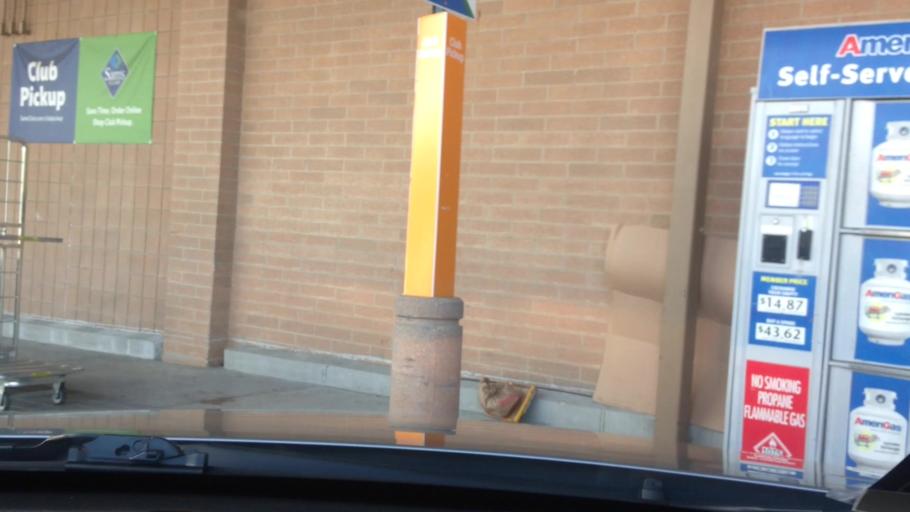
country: US
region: Missouri
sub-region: Clay County
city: Gladstone
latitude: 39.1864
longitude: -94.5789
